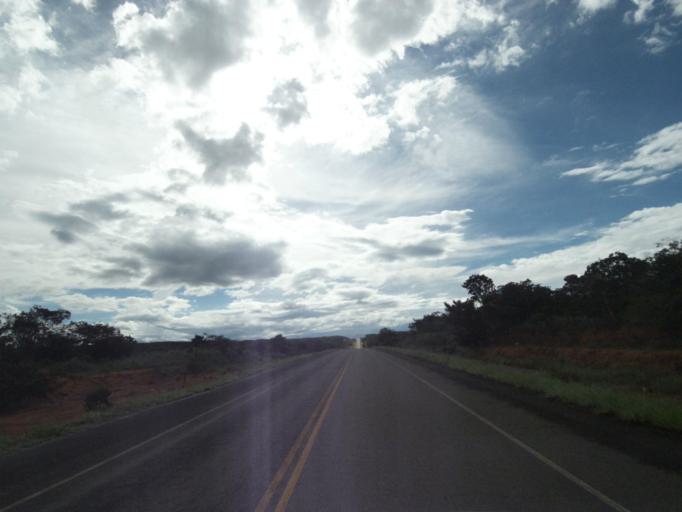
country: BR
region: Goias
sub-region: Jaragua
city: Jaragua
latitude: -15.8398
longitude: -49.2920
